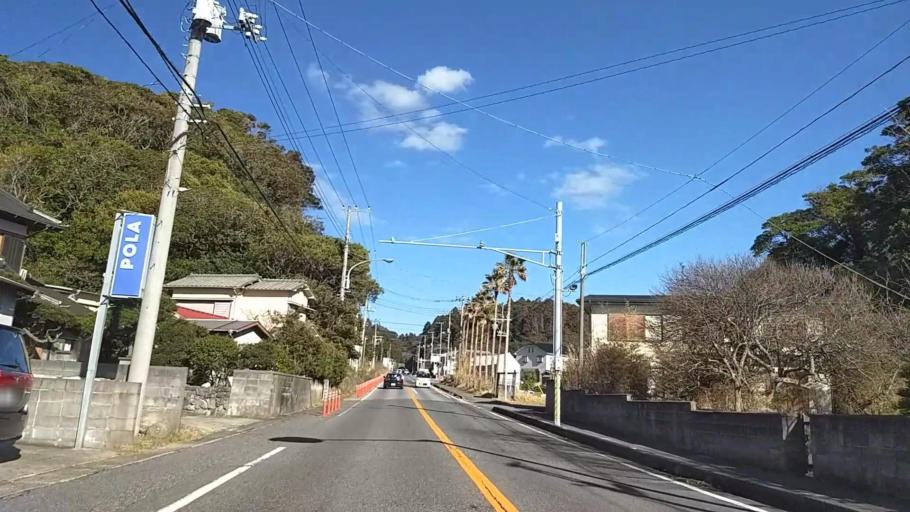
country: JP
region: Chiba
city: Ohara
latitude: 35.1928
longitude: 140.3621
